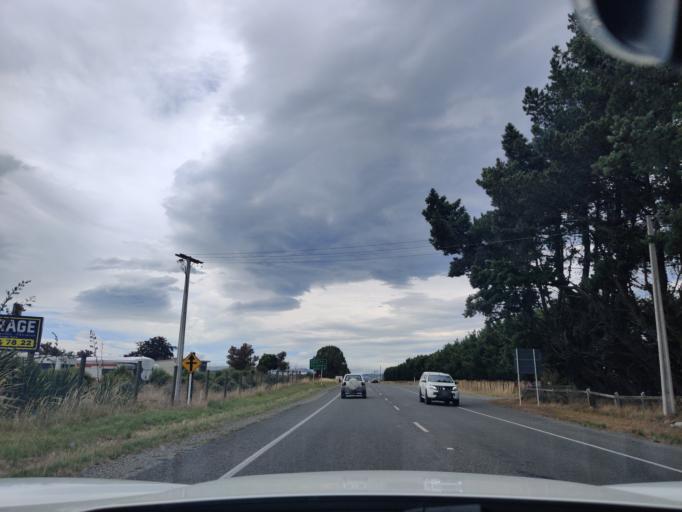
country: NZ
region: Wellington
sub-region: Masterton District
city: Masterton
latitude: -40.9725
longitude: 175.5984
